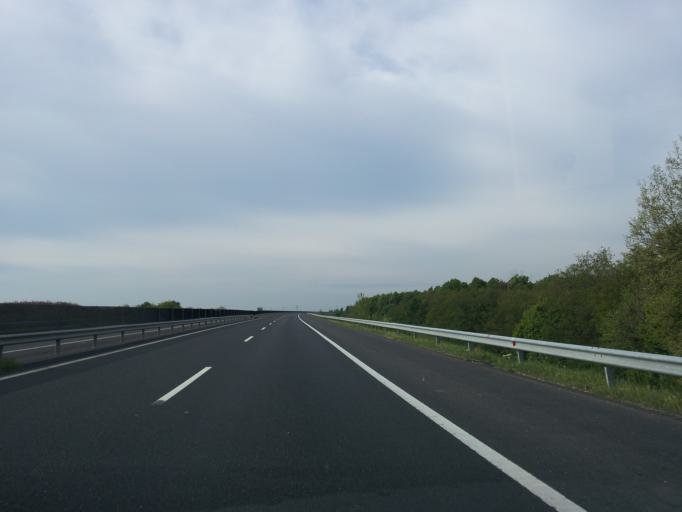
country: HU
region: Fejer
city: Ivancsa
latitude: 47.2039
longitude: 18.8177
